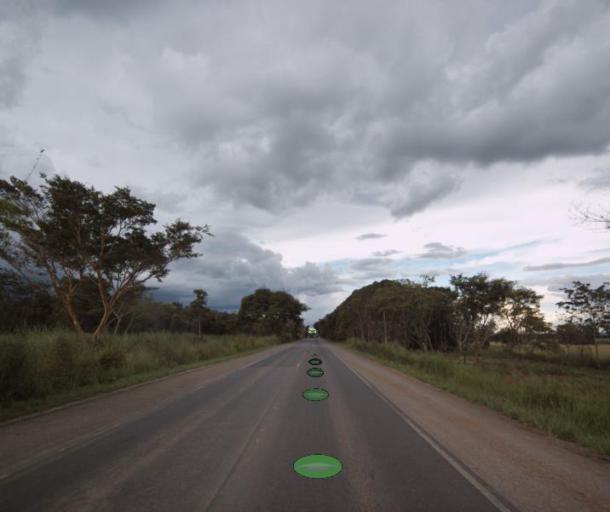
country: BR
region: Goias
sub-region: Itapaci
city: Itapaci
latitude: -15.0707
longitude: -49.4570
